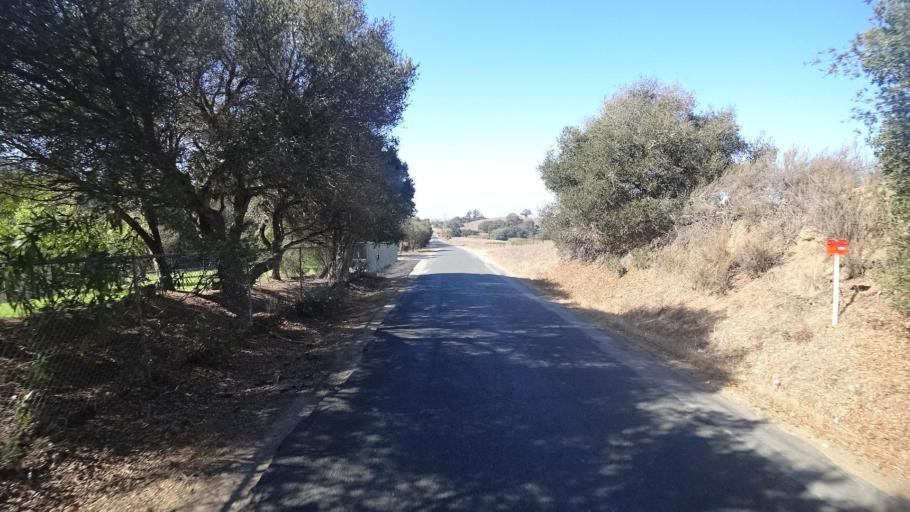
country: US
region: California
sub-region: Monterey County
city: Prunedale
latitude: 36.7758
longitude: -121.6002
